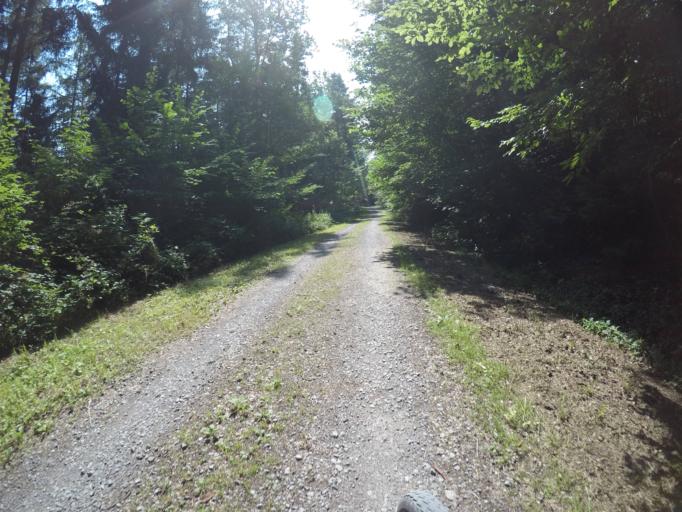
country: DE
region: Baden-Wuerttemberg
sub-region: Regierungsbezirk Stuttgart
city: Schlaitdorf
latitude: 48.6264
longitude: 9.1941
